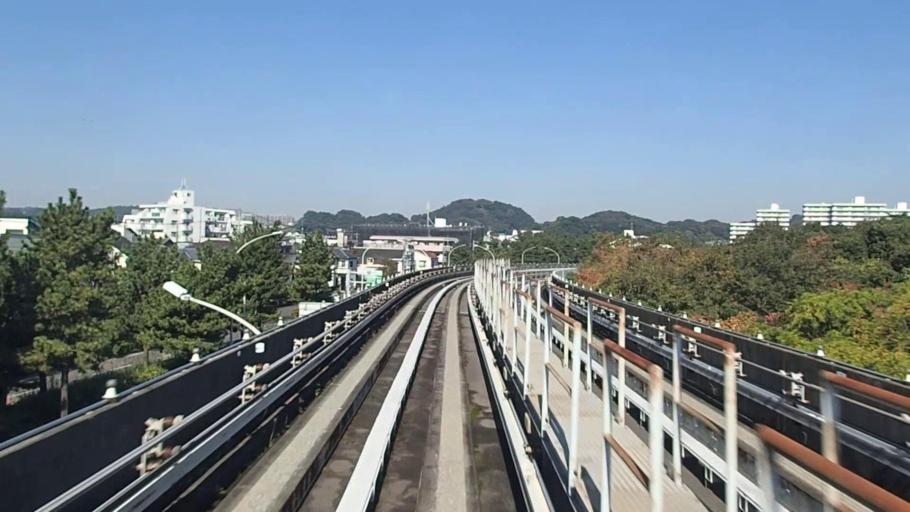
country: JP
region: Kanagawa
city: Yokosuka
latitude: 35.3358
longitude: 139.6321
